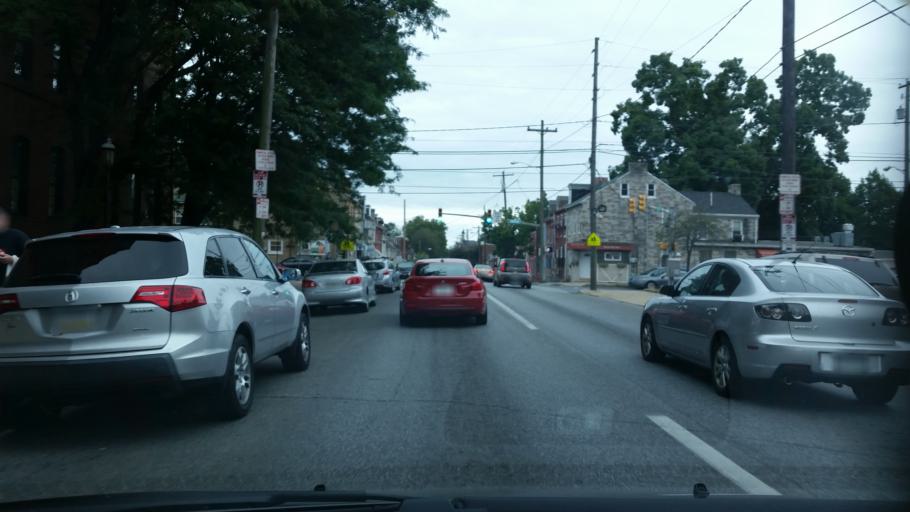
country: US
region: Pennsylvania
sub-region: Lancaster County
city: Lancaster
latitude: 40.0334
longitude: -76.3069
